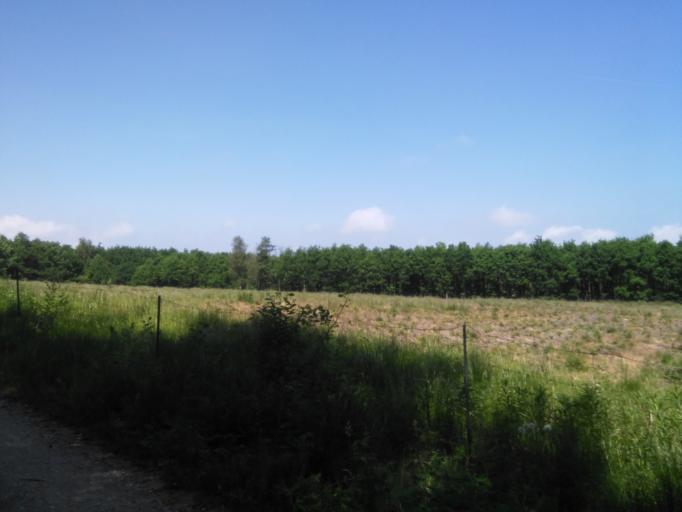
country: DK
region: Central Jutland
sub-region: Arhus Kommune
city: Solbjerg
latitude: 55.9546
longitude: 10.0460
